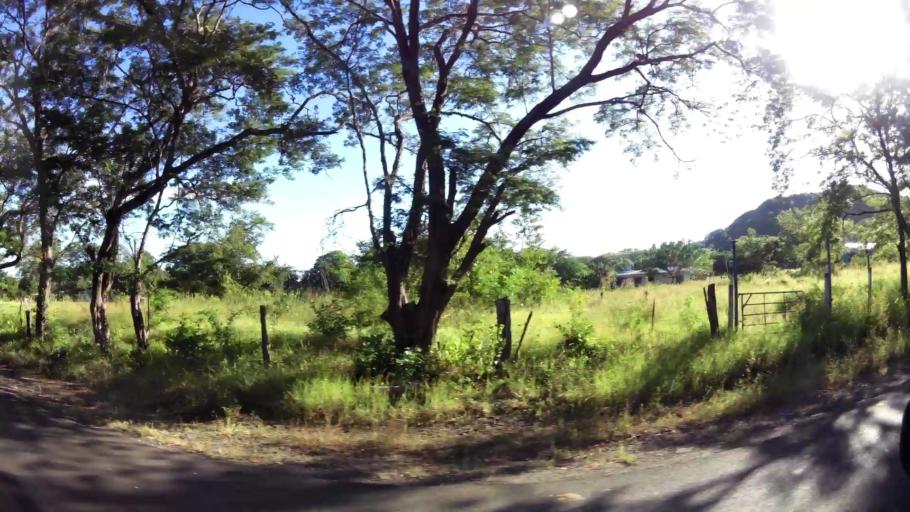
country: CR
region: Guanacaste
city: Sardinal
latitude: 10.5040
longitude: -85.6466
